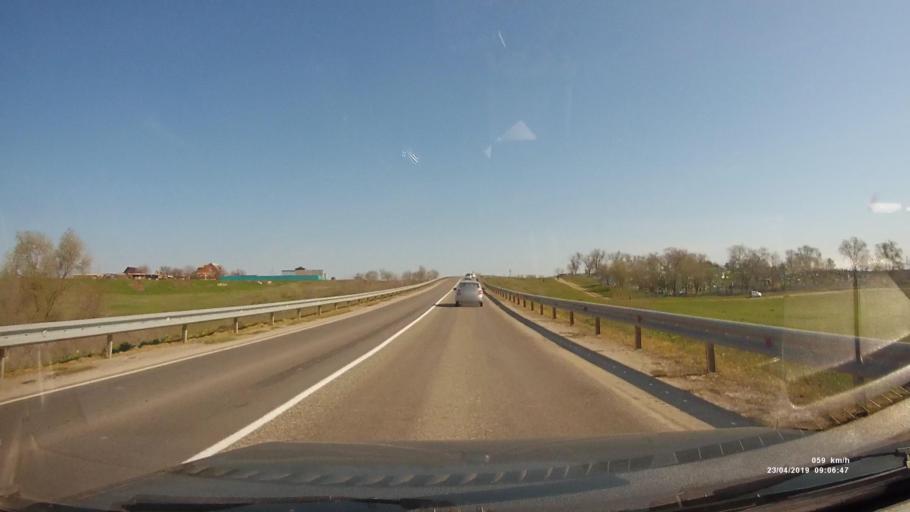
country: RU
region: Rostov
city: Sal'sk
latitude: 46.5506
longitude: 41.5890
